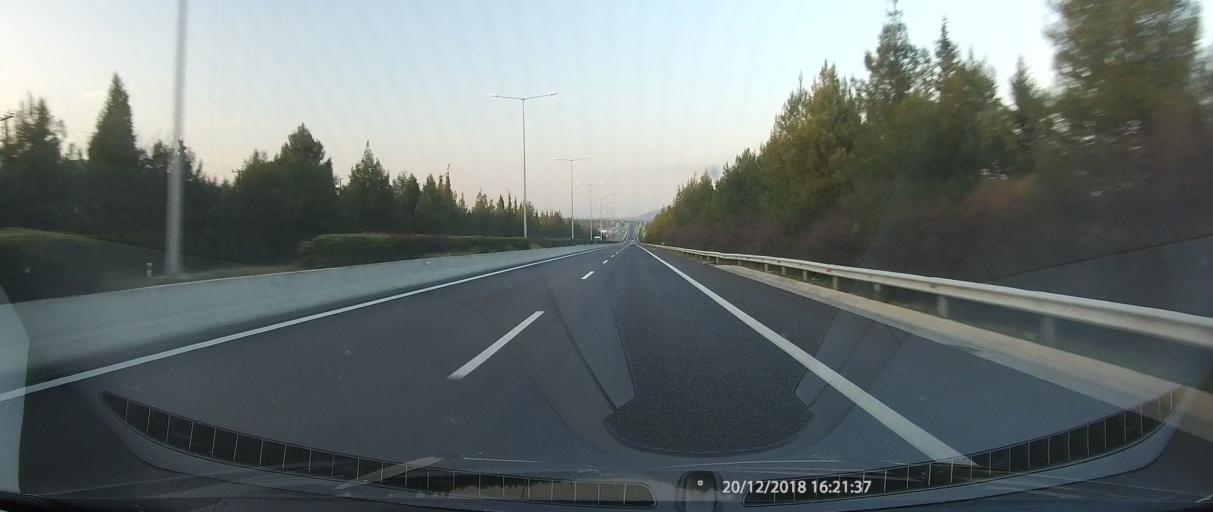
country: GR
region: Thessaly
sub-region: Nomos Magnisias
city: Sourpi
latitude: 39.0520
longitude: 22.8918
